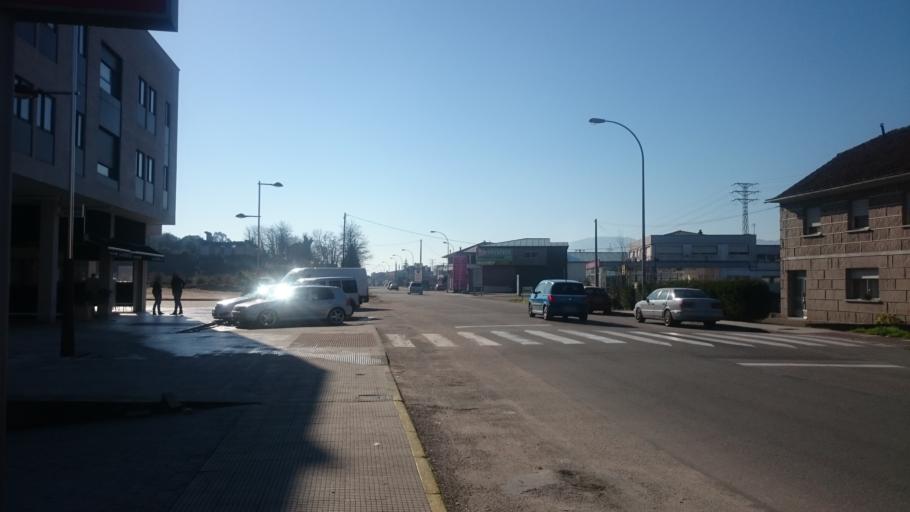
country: ES
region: Galicia
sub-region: Provincia de Pontevedra
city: Porrino
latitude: 42.1523
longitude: -8.6209
